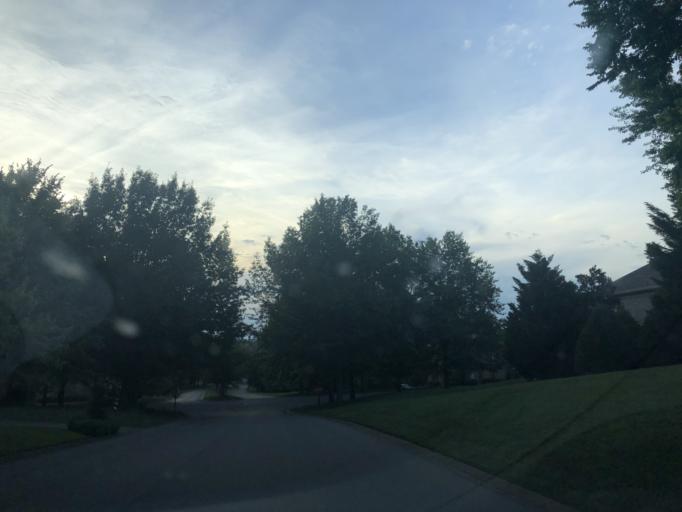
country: US
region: Tennessee
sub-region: Davidson County
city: Forest Hills
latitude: 36.0470
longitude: -86.9212
